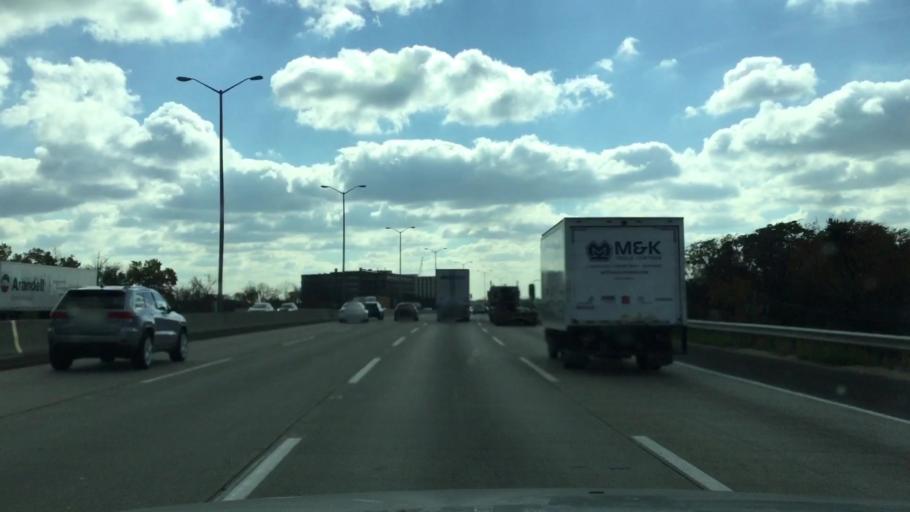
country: US
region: Illinois
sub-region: Cook County
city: Des Plaines
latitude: 42.0839
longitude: -87.8663
